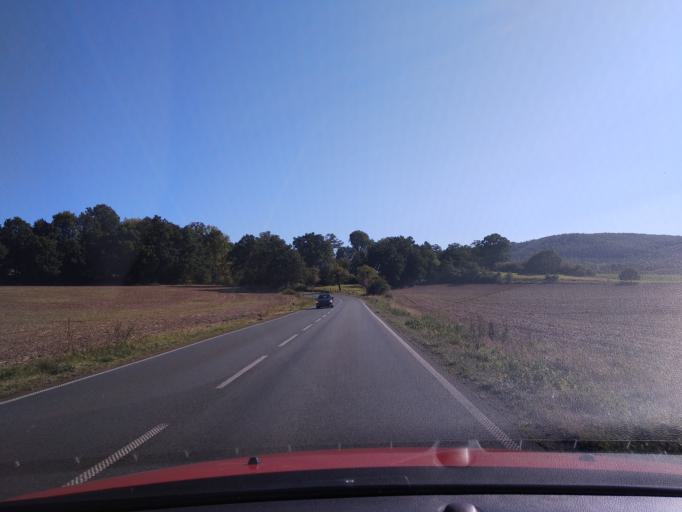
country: DE
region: Lower Saxony
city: Boffzen
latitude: 51.7257
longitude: 9.3709
